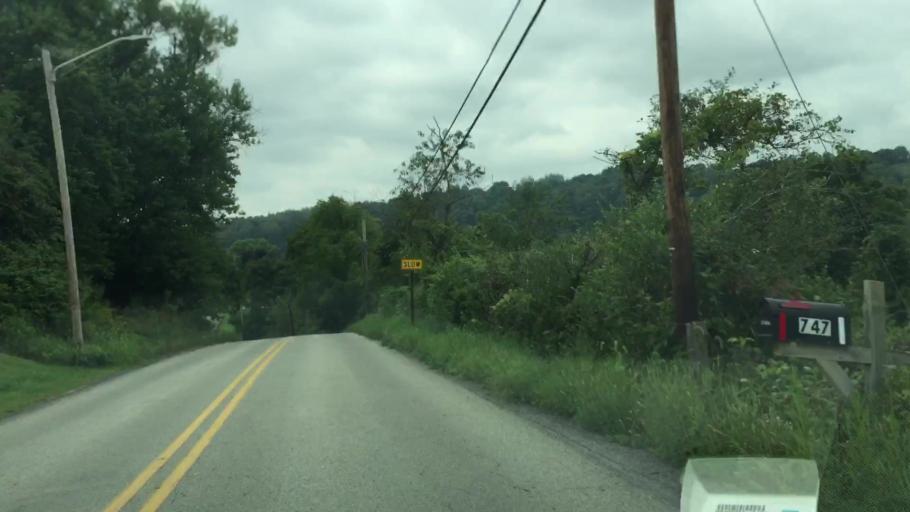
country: US
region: Pennsylvania
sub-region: Allegheny County
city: Oakdale
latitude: 40.4114
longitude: -80.1898
